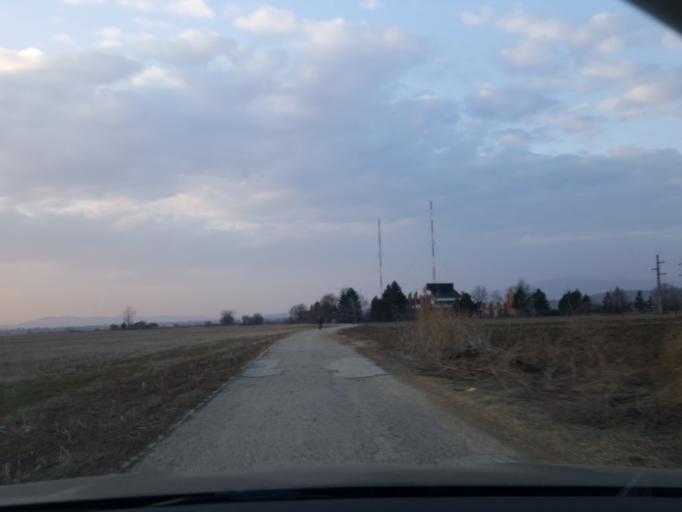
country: RS
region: Central Serbia
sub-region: Nisavski Okrug
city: Aleksinac
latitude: 43.5483
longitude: 21.6718
